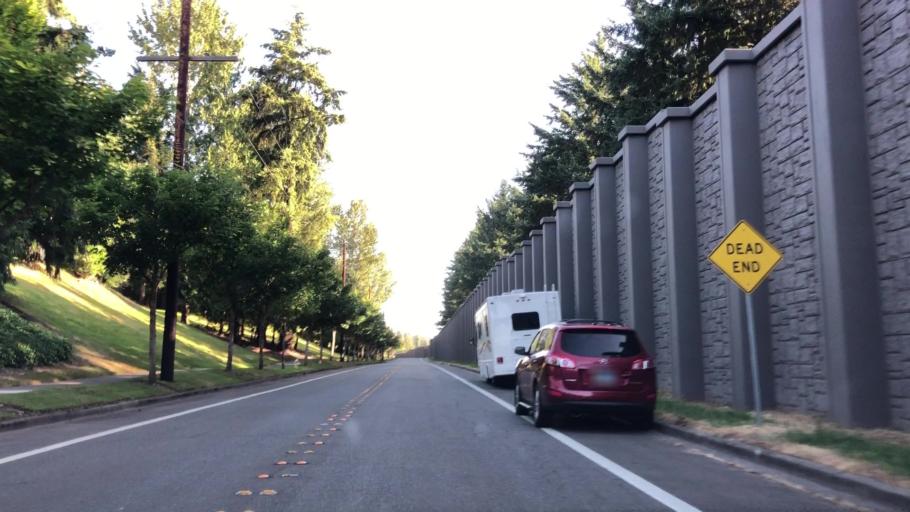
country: US
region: Washington
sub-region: King County
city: Bothell
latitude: 47.7701
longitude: -122.1909
